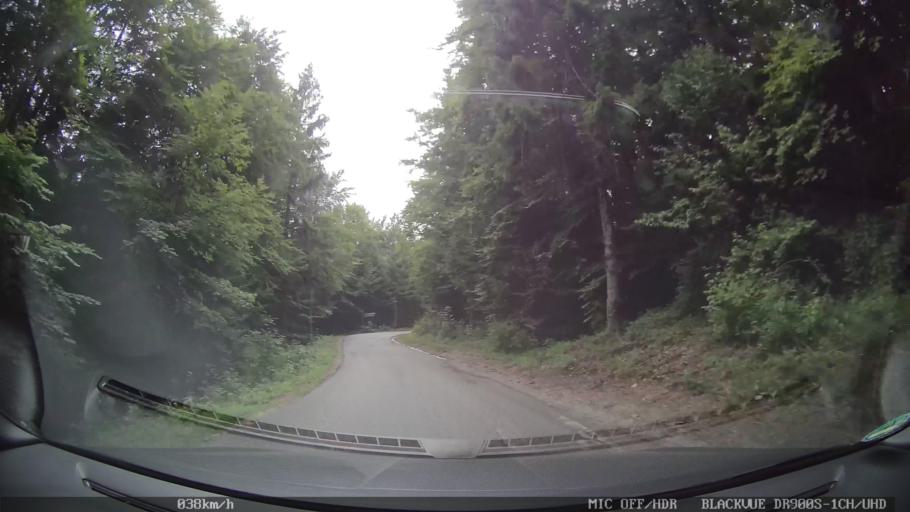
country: HR
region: Licko-Senjska
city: Jezerce
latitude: 44.9261
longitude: 15.5708
